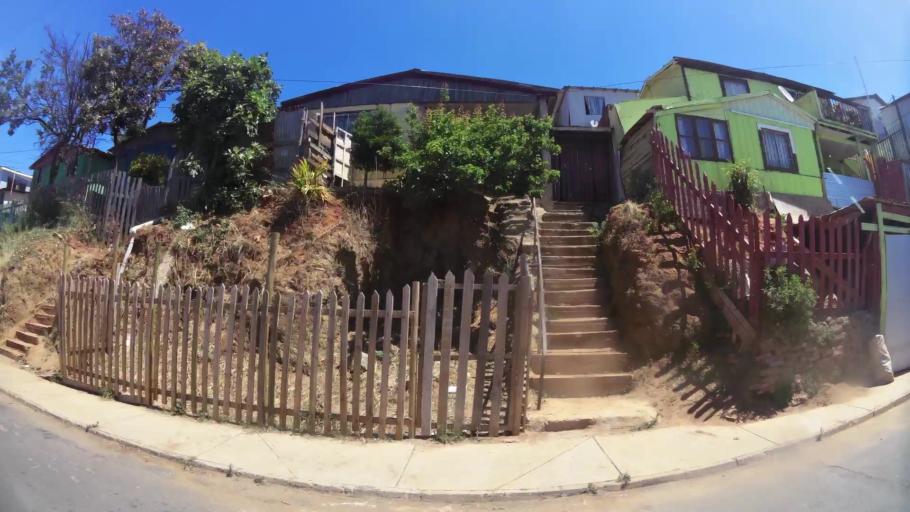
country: CL
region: Valparaiso
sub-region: Provincia de Valparaiso
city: Valparaiso
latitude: -33.0544
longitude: -71.6386
